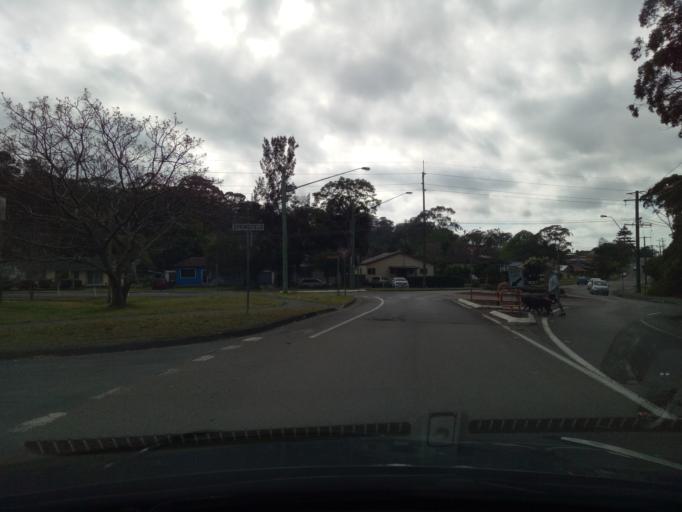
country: AU
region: New South Wales
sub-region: Gosford Shire
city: East Gosford
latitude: -33.4313
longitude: 151.3581
